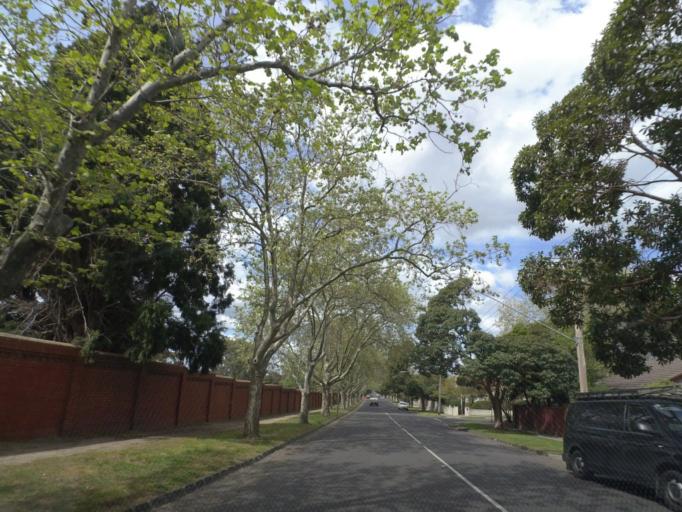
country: AU
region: Victoria
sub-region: Boroondara
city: Kew East
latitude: -37.8044
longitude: 145.0439
